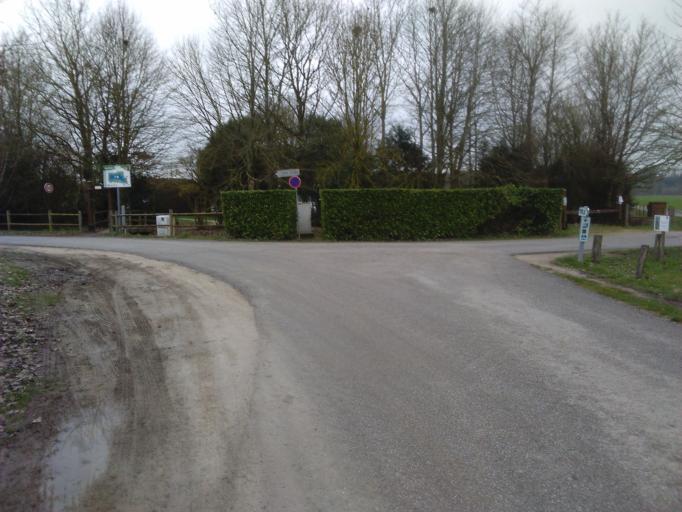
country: FR
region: Centre
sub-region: Departement du Loir-et-Cher
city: Villiers-sur-Loir
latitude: 47.8027
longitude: 0.9907
